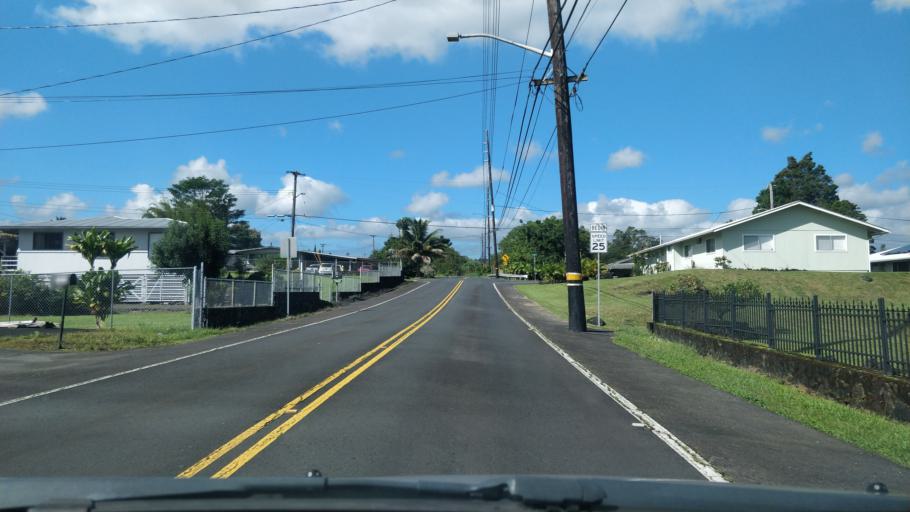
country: US
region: Hawaii
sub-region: Hawaii County
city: Hilo
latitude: 19.6821
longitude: -155.1035
